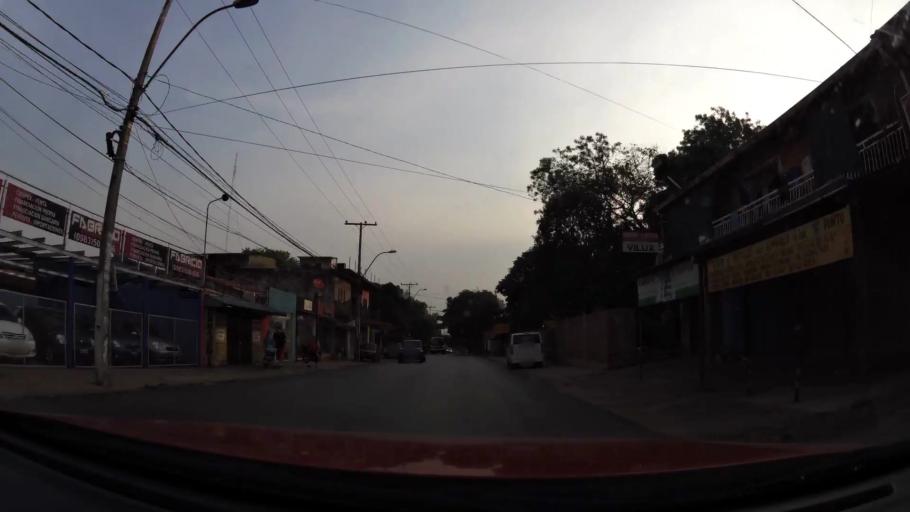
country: PY
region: Central
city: Lambare
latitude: -25.3242
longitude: -57.5809
